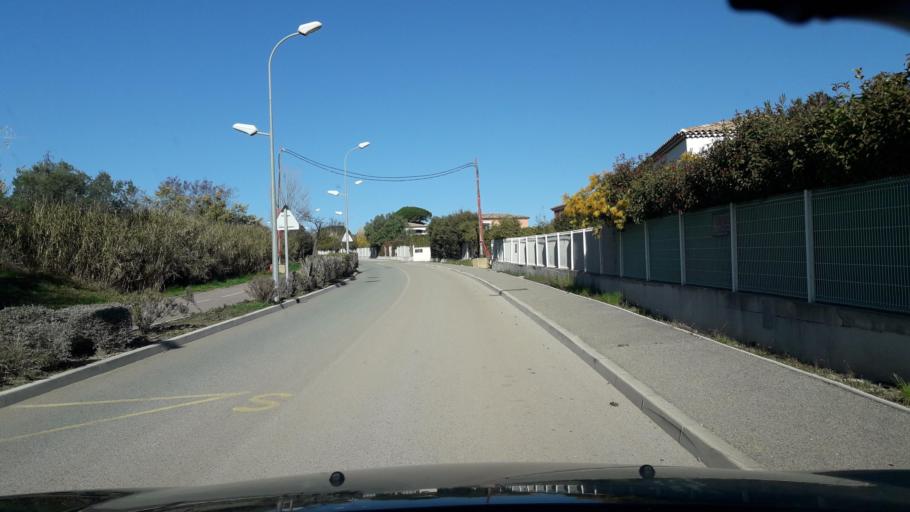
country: FR
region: Provence-Alpes-Cote d'Azur
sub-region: Departement du Var
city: Saint-Raphael
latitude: 43.4424
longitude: 6.7599
